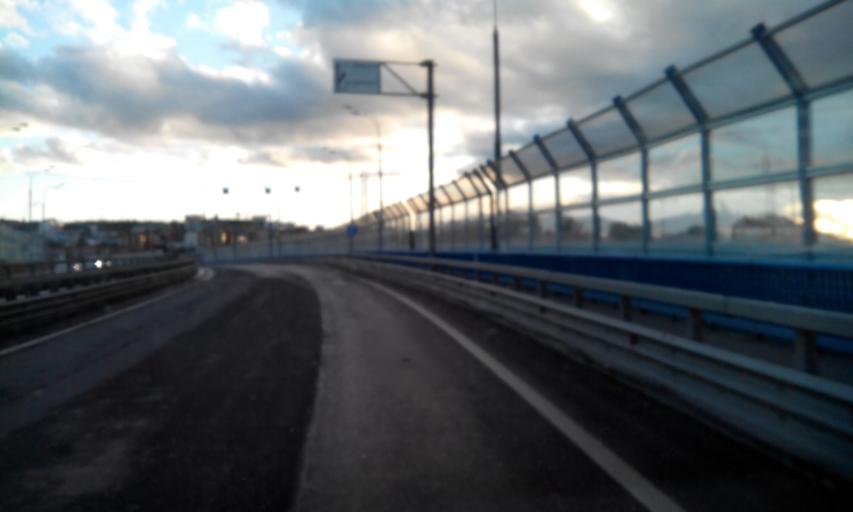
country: RU
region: Penza
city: Penza
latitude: 53.1907
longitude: 45.0348
